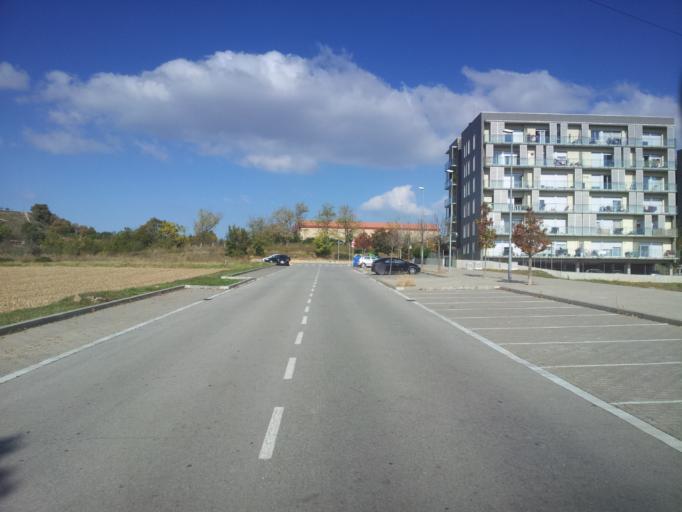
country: ES
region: Catalonia
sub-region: Provincia de Barcelona
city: Vic
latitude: 41.9306
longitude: 2.2388
